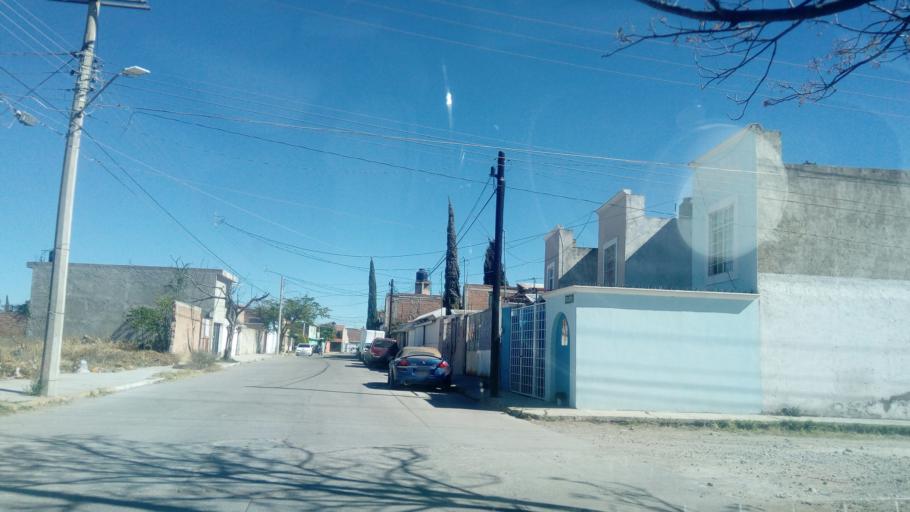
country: MX
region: Durango
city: Victoria de Durango
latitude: 24.0166
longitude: -104.6425
